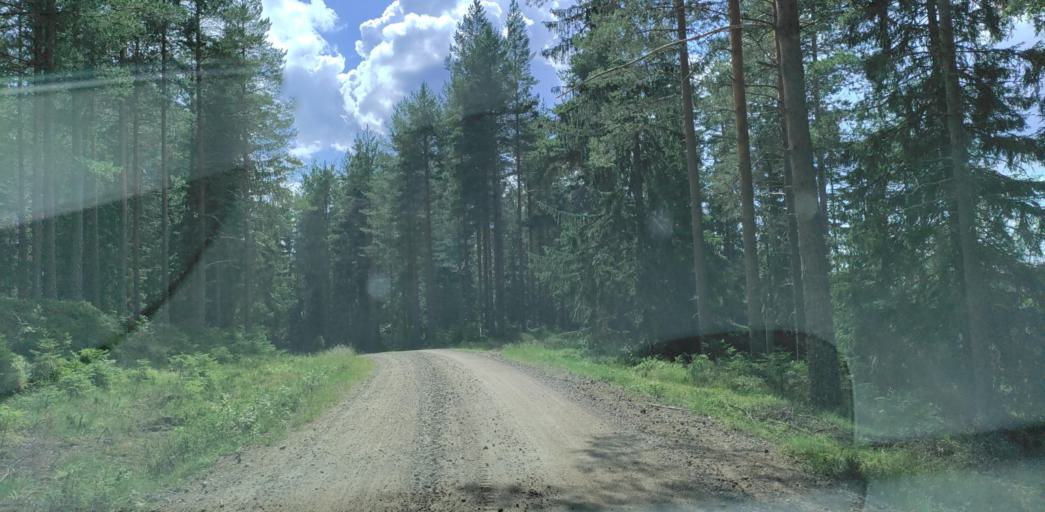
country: SE
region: Vaermland
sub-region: Hagfors Kommun
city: Ekshaerad
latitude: 60.0846
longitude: 13.3451
